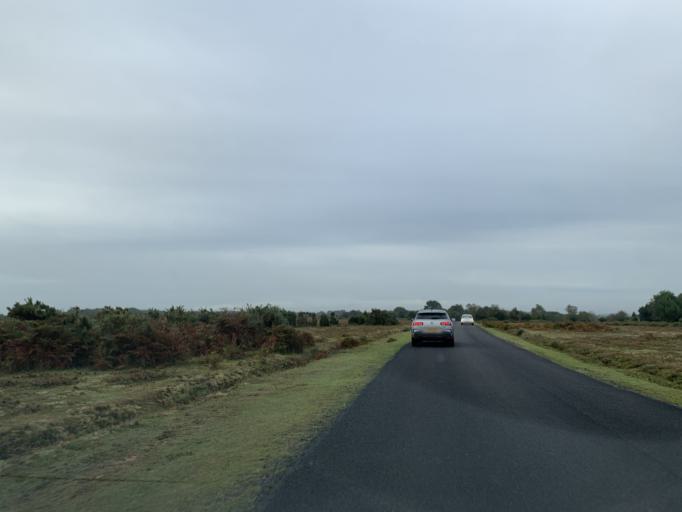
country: GB
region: England
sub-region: Wiltshire
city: Whiteparish
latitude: 50.9441
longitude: -1.6481
